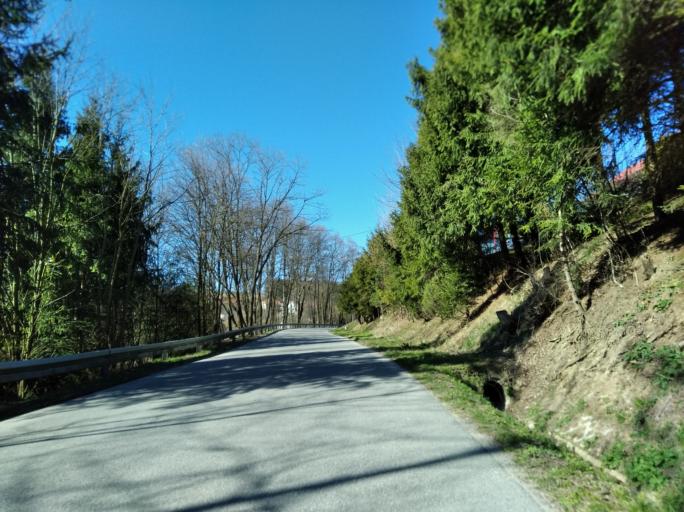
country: PL
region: Subcarpathian Voivodeship
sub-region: Powiat strzyzowski
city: Wisniowa
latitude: 49.8895
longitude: 21.6670
